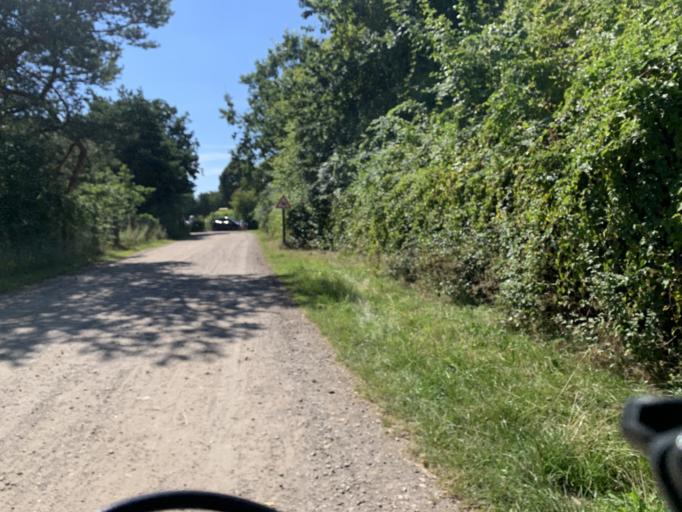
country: DE
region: Lower Saxony
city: Wietzendorf
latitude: 52.9344
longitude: 9.9746
